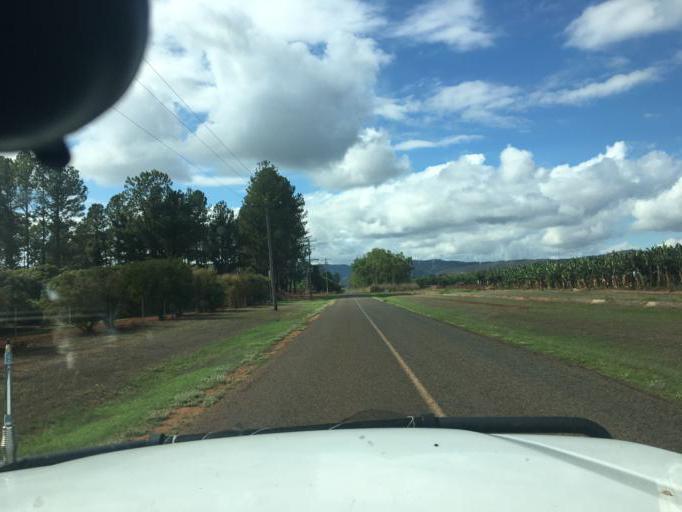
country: AU
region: Queensland
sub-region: Tablelands
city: Mareeba
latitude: -17.1058
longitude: 145.4112
